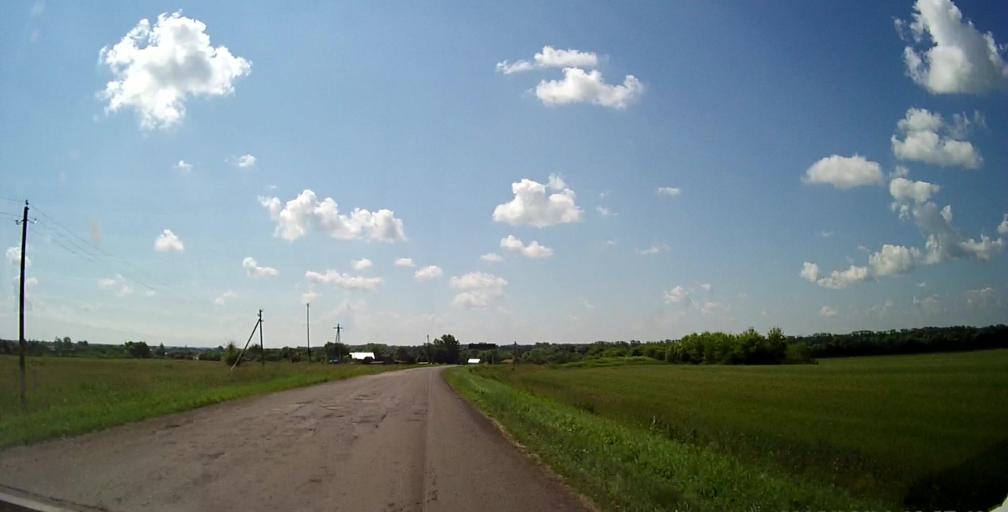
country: RU
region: Lipetsk
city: Chaplygin
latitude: 53.3553
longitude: 39.9244
